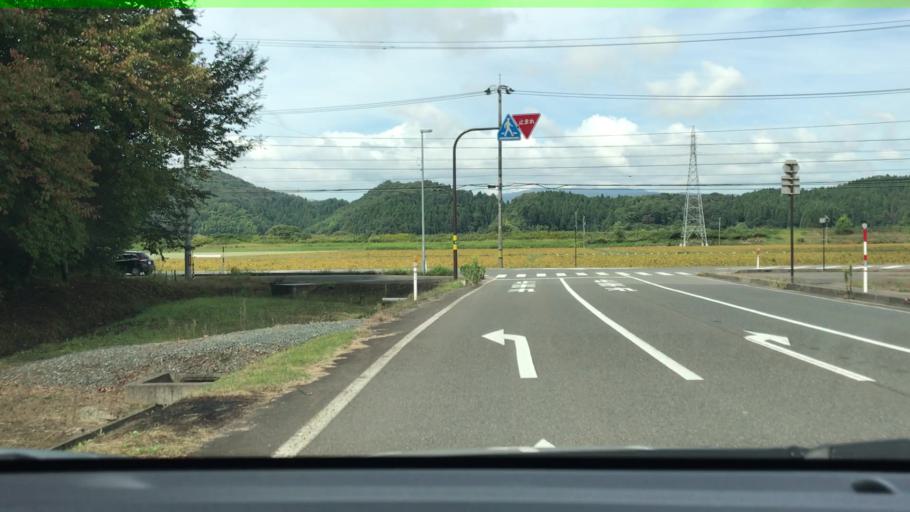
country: JP
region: Fukui
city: Fukui-shi
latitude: 36.0231
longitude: 136.1794
